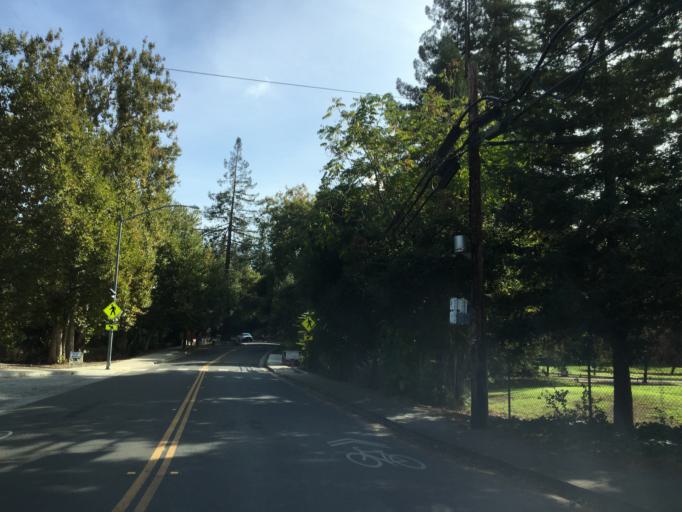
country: US
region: California
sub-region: Santa Clara County
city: Cupertino
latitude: 37.3133
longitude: -122.0651
